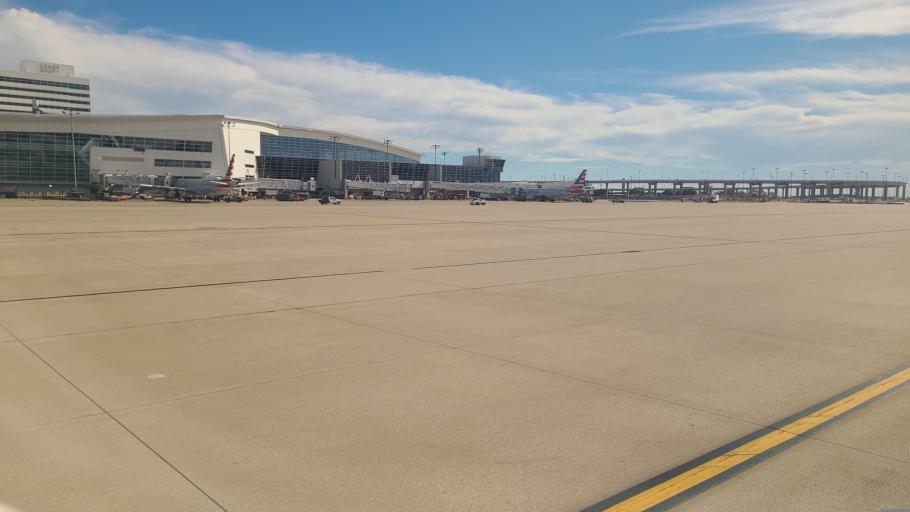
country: US
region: Texas
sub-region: Tarrant County
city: Grapevine
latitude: 32.8977
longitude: -97.0479
